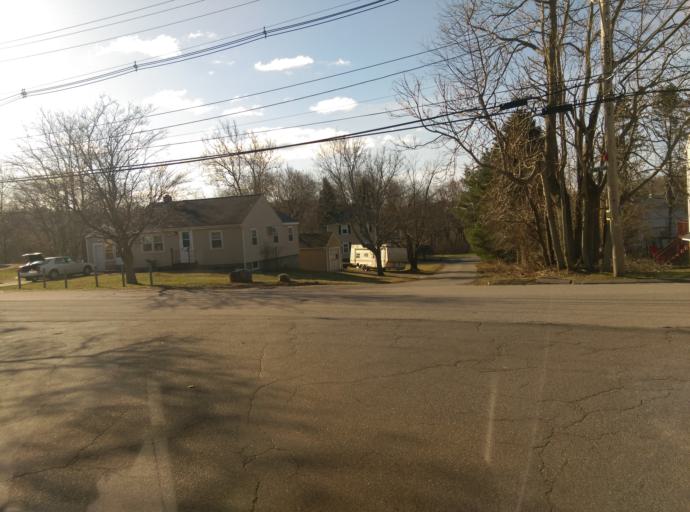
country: US
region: Massachusetts
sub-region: Essex County
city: Haverhill
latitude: 42.7491
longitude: -71.1121
